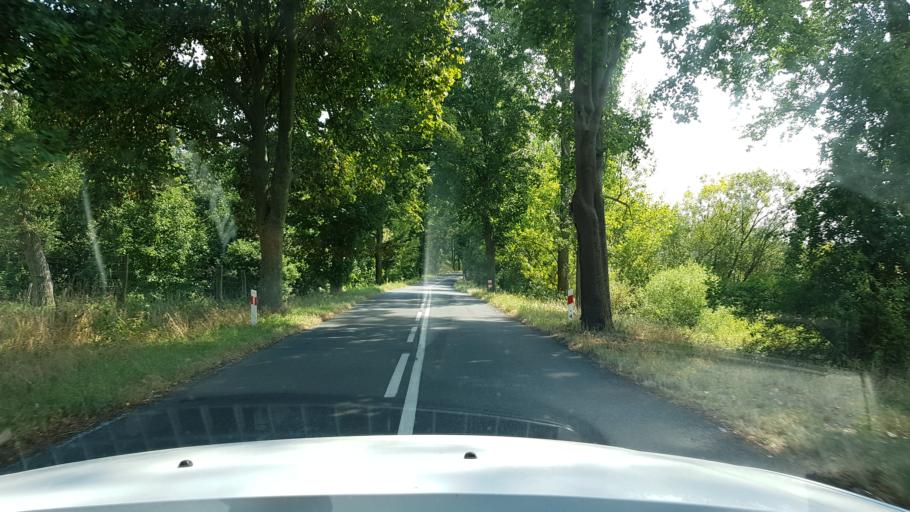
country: PL
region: West Pomeranian Voivodeship
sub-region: Powiat gryfinski
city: Cedynia
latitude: 52.8252
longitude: 14.2253
